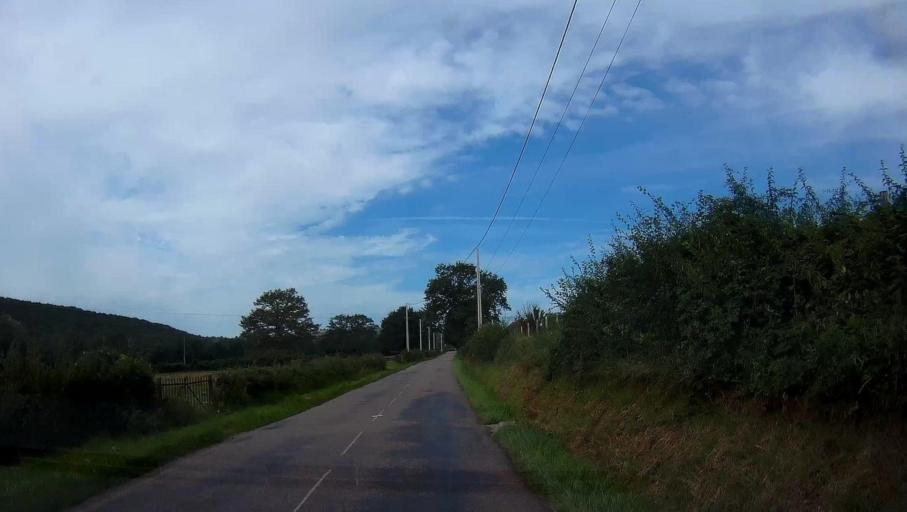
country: FR
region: Bourgogne
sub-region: Departement de Saone-et-Loire
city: Saint-Leger-sur-Dheune
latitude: 46.8689
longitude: 4.6217
